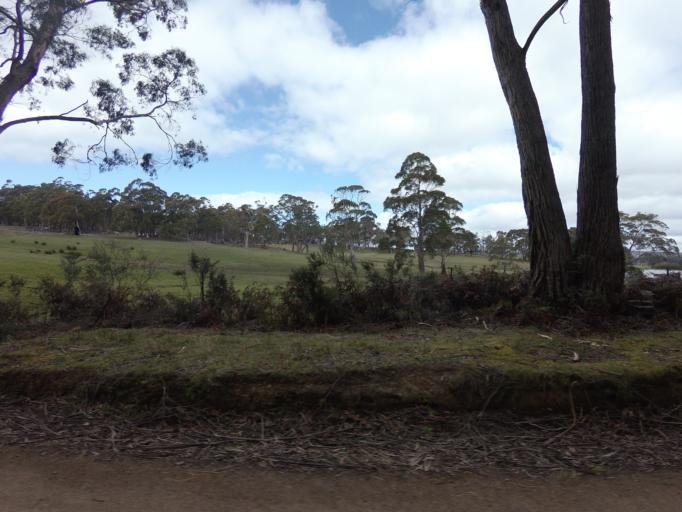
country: AU
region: Tasmania
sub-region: Huon Valley
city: Geeveston
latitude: -43.4255
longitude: 146.9997
